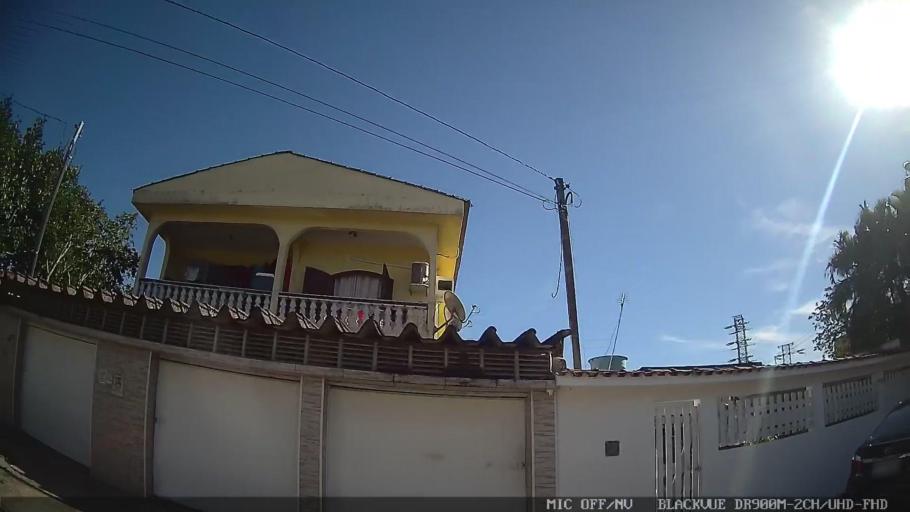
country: BR
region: Sao Paulo
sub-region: Santos
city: Santos
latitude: -23.9359
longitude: -46.2861
